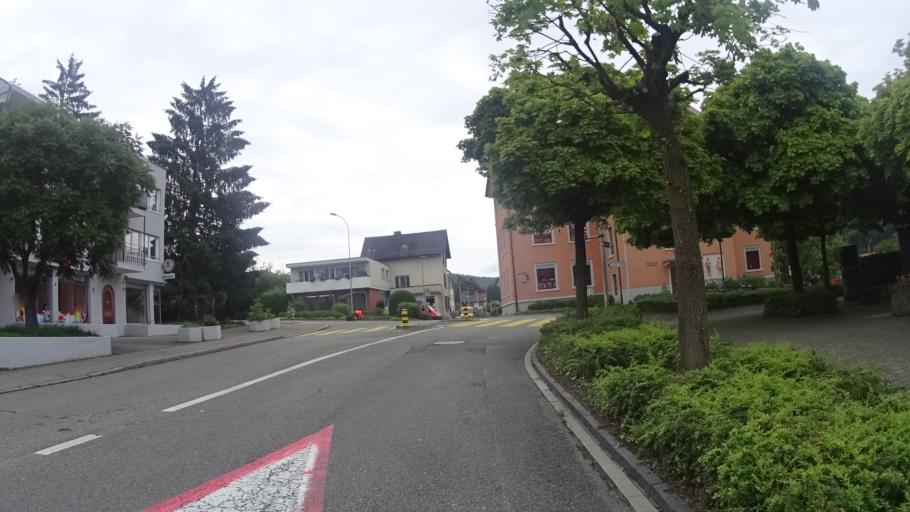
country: CH
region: Aargau
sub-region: Bezirk Baden
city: Obersiggenthal
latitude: 47.4885
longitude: 8.2936
